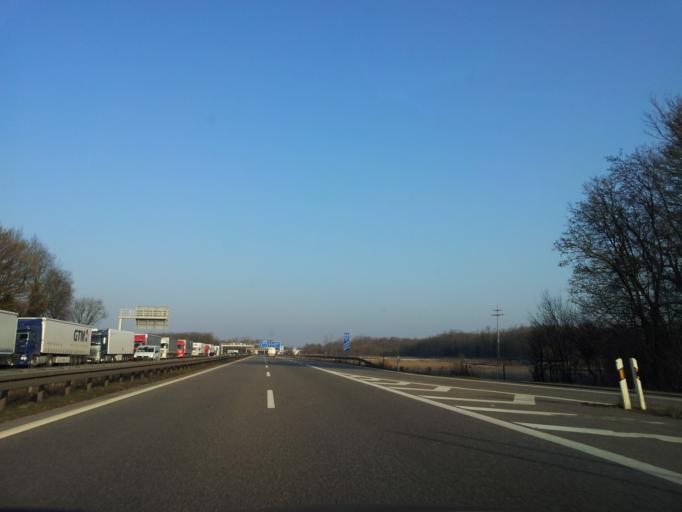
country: FR
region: Alsace
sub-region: Departement du Haut-Rhin
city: Huningue
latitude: 47.6128
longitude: 7.5912
